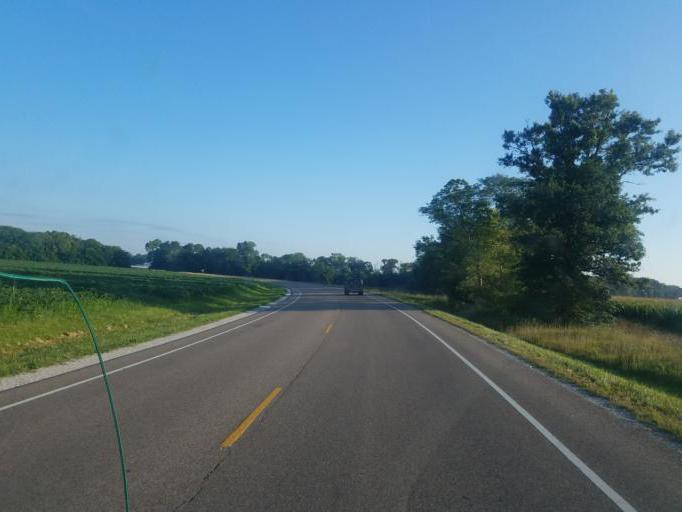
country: US
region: Illinois
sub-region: Bond County
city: Greenville
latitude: 38.8587
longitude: -89.3715
